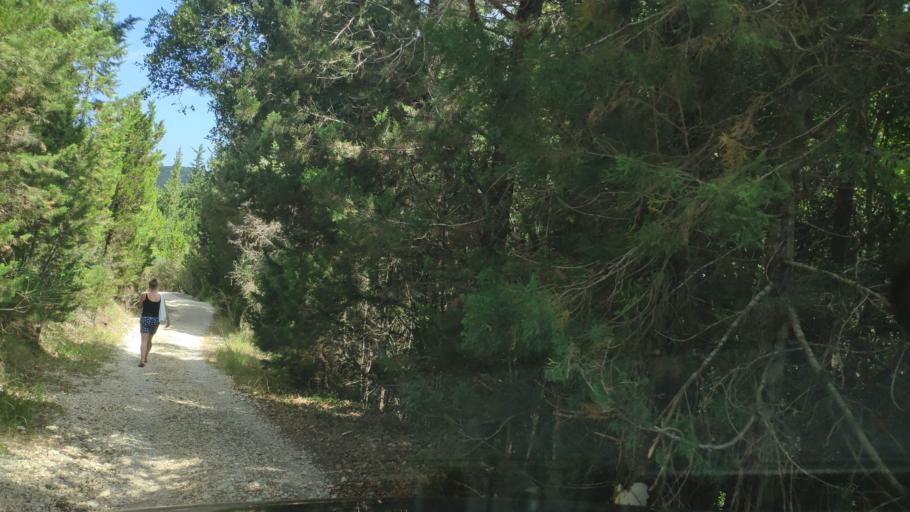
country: GR
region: Ionian Islands
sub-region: Lefkada
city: Lefkada
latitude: 38.7977
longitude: 20.6737
